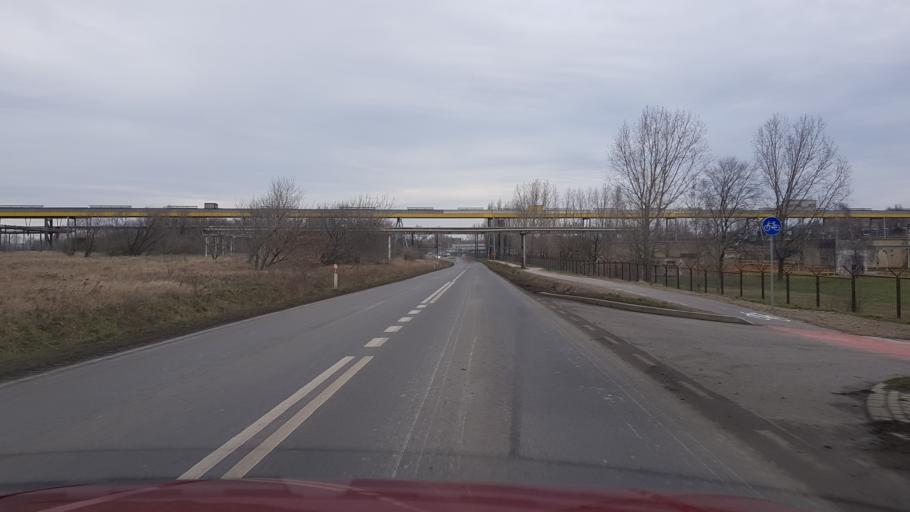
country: PL
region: West Pomeranian Voivodeship
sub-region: Powiat policki
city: Police
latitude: 53.5743
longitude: 14.5557
